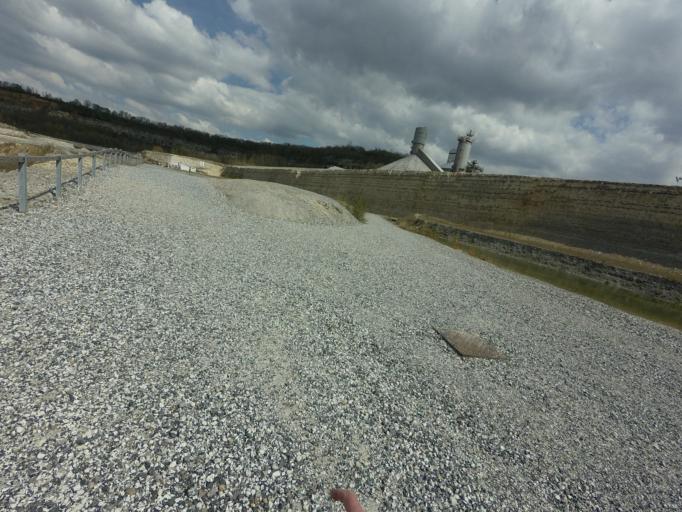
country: NL
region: Limburg
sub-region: Gemeente Maastricht
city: Maastricht
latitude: 50.8204
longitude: 5.6880
